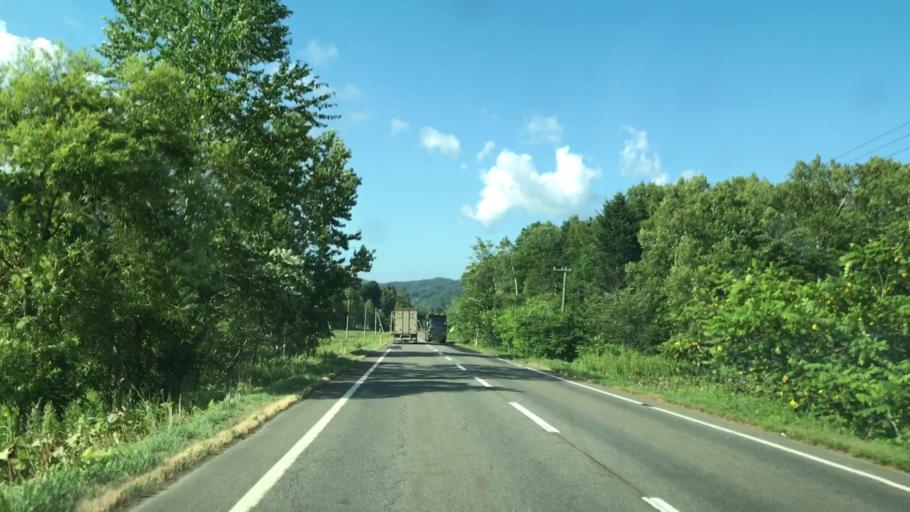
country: JP
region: Hokkaido
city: Shimo-furano
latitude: 42.8635
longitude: 142.4230
